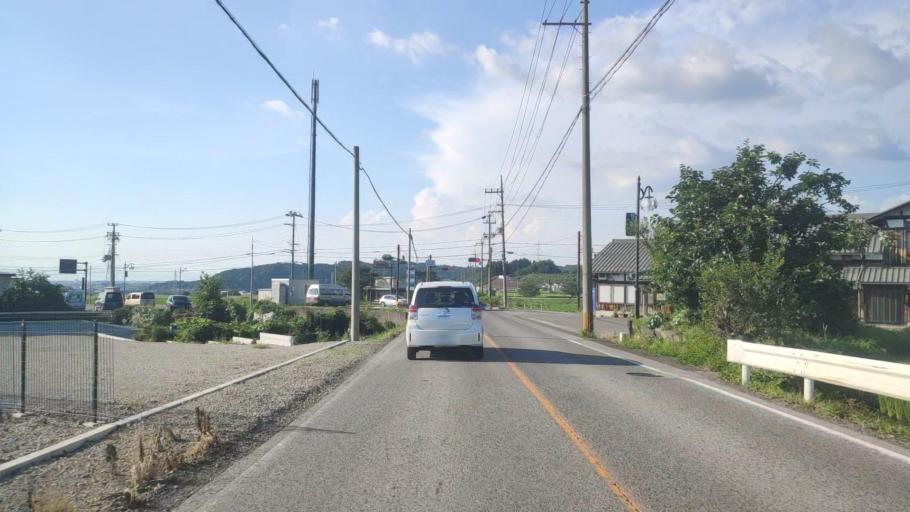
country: JP
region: Shiga Prefecture
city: Youkaichi
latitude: 35.1592
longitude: 136.2725
